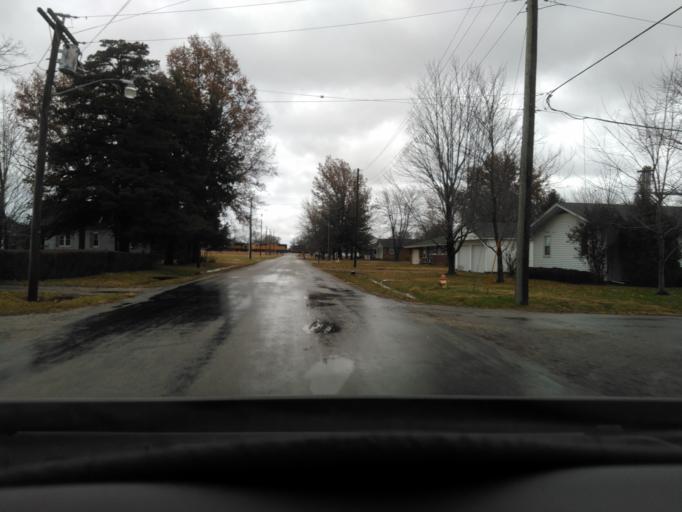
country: US
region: Illinois
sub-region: Effingham County
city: Altamont
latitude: 39.0564
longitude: -88.7564
